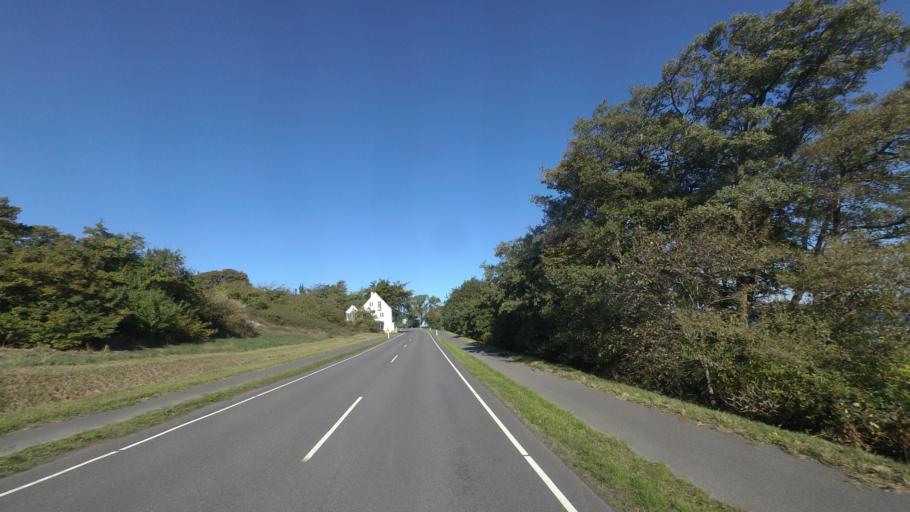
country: DK
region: Capital Region
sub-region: Bornholm Kommune
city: Akirkeby
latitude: 55.1770
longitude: 15.0197
